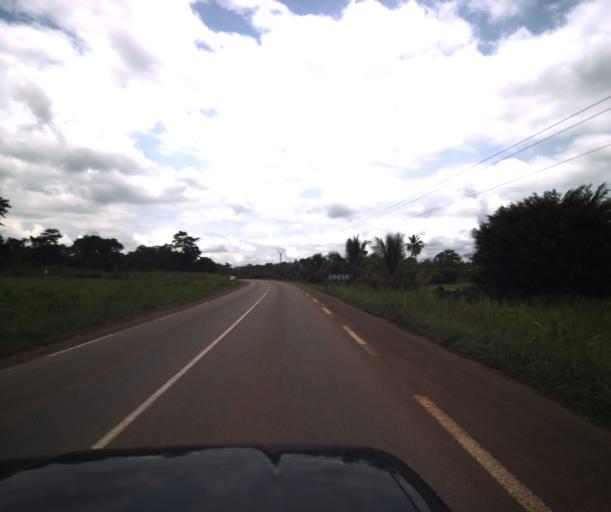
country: CM
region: Centre
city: Eseka
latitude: 3.8598
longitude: 10.9340
